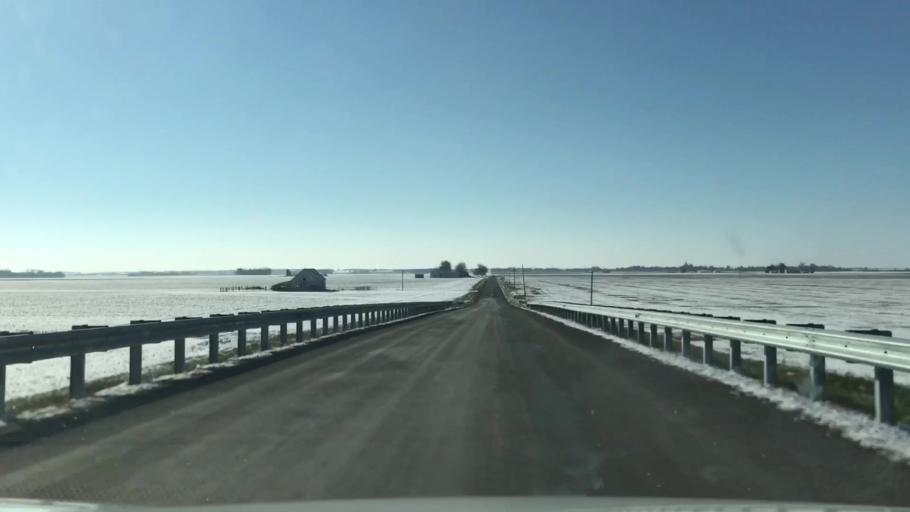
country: US
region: Illinois
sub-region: Washington County
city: Okawville
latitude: 38.4265
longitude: -89.4778
